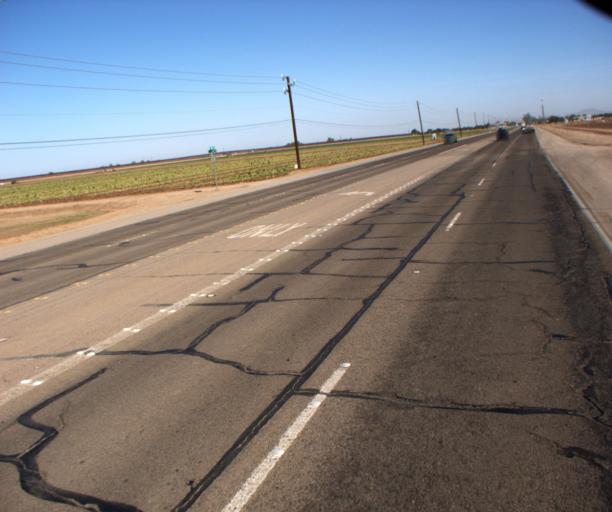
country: US
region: Arizona
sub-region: Yuma County
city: San Luis
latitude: 32.5375
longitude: -114.7868
